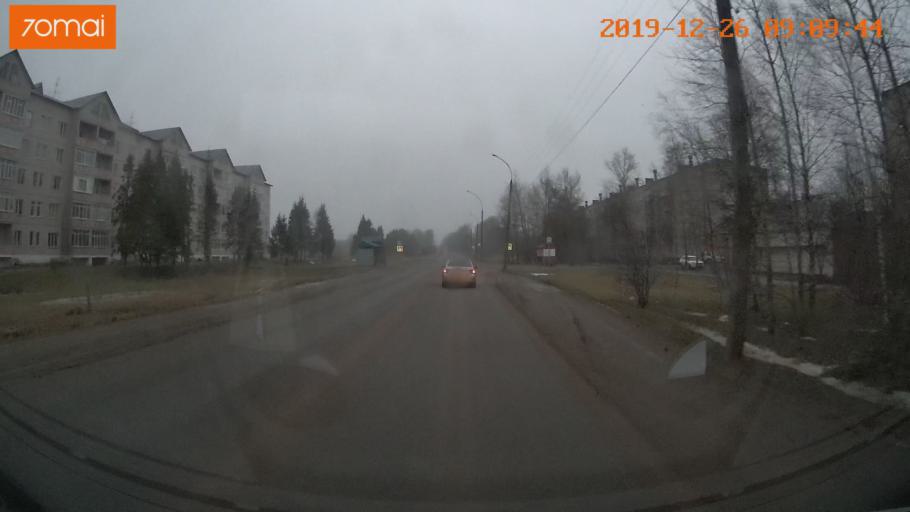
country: RU
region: Vologda
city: Gryazovets
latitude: 58.8661
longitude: 40.2527
